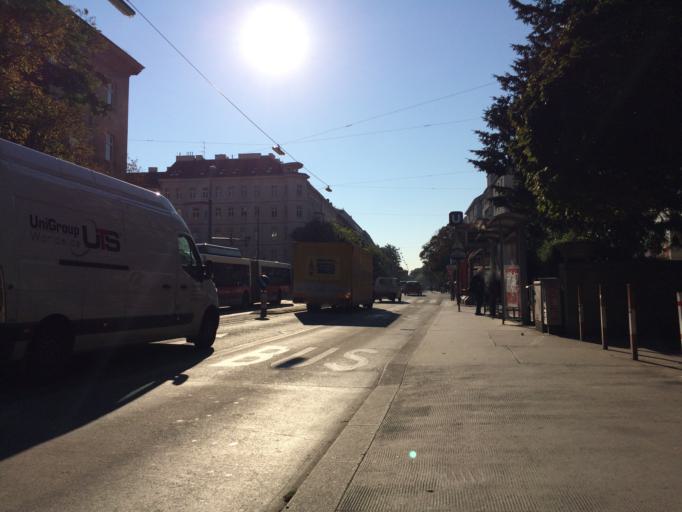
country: AT
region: Vienna
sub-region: Wien Stadt
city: Vienna
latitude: 48.2246
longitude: 16.4013
